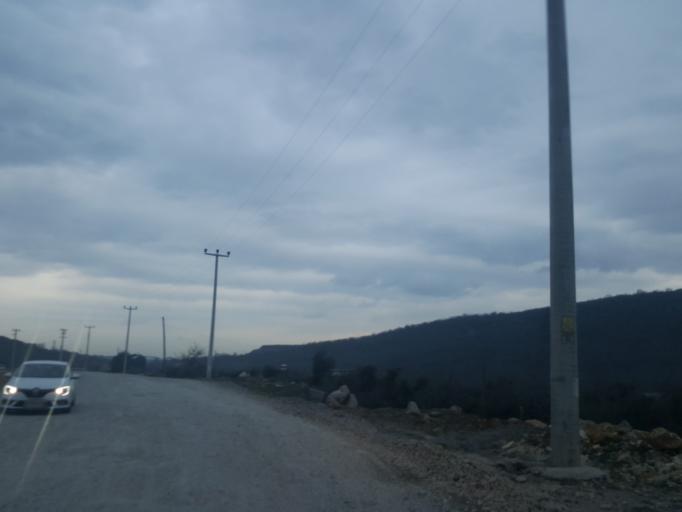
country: TR
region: Kocaeli
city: Tavsanli
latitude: 40.8586
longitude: 29.5720
